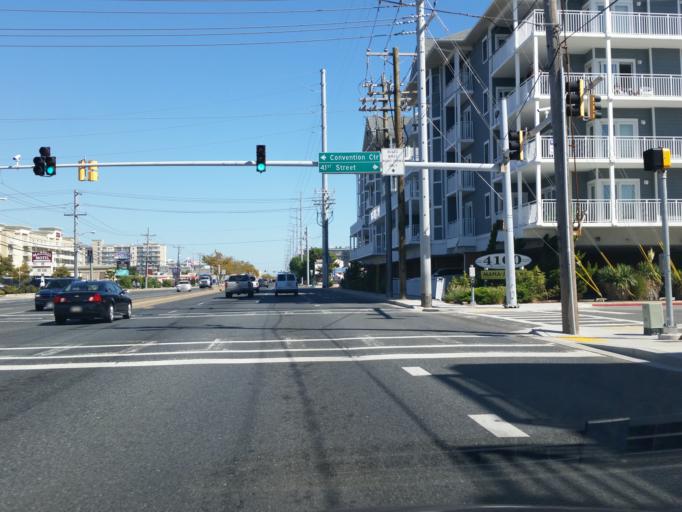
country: US
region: Maryland
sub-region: Worcester County
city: Ocean City
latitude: 38.3678
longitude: -75.0712
